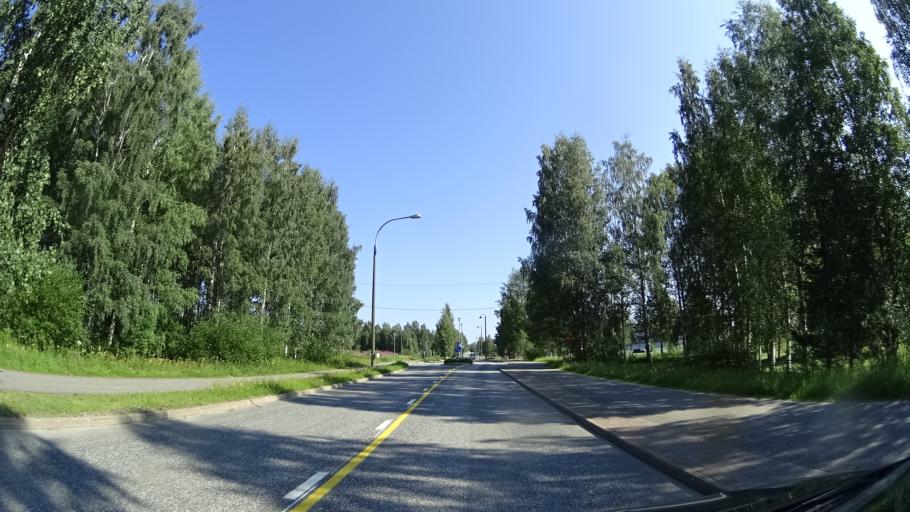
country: FI
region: North Karelia
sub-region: Joensuu
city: Juuka
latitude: 63.2365
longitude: 29.2479
